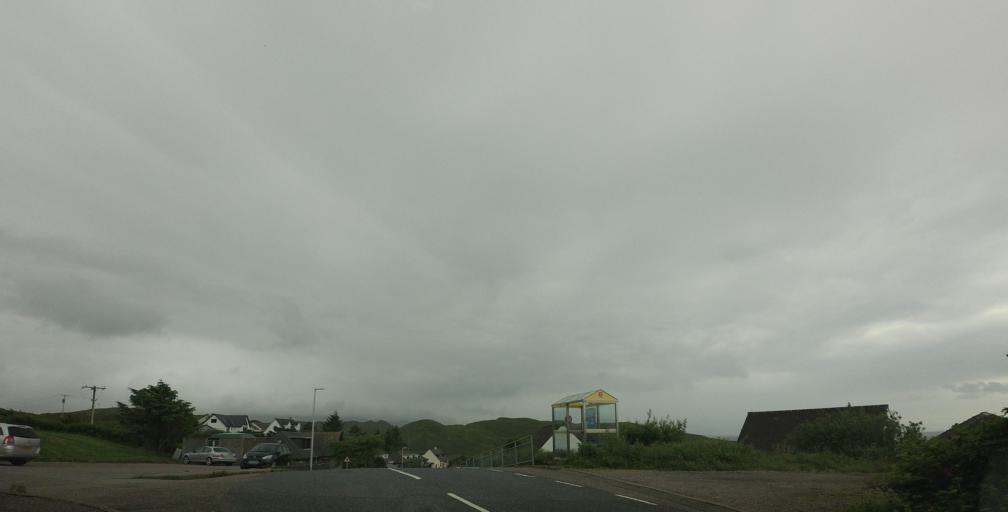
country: GB
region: Scotland
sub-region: Argyll and Bute
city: Isle Of Mull
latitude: 56.9970
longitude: -5.8293
